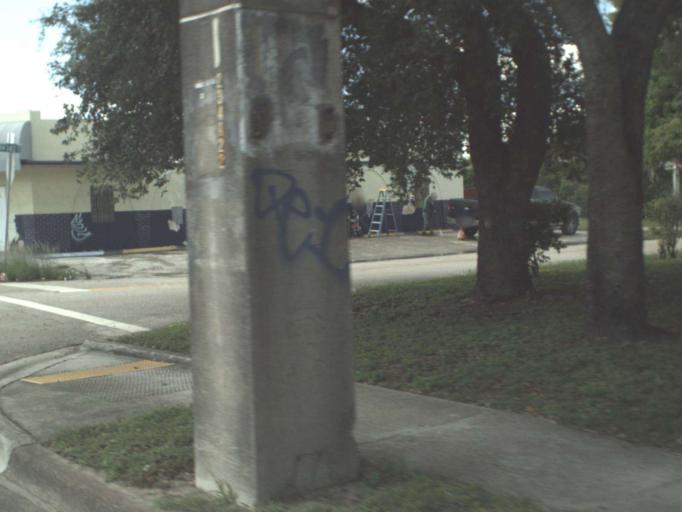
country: US
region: Florida
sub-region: Miami-Dade County
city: Golden Glades
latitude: 25.9028
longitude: -80.2116
